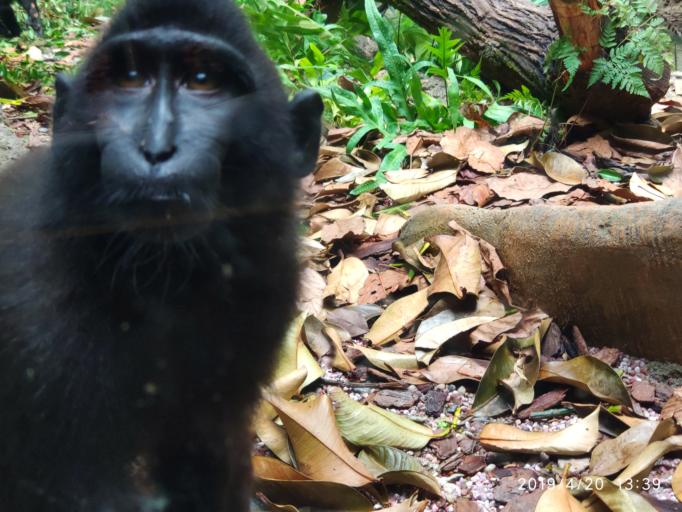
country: MY
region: Johor
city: Johor Bahru
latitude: 1.4022
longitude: 103.7959
